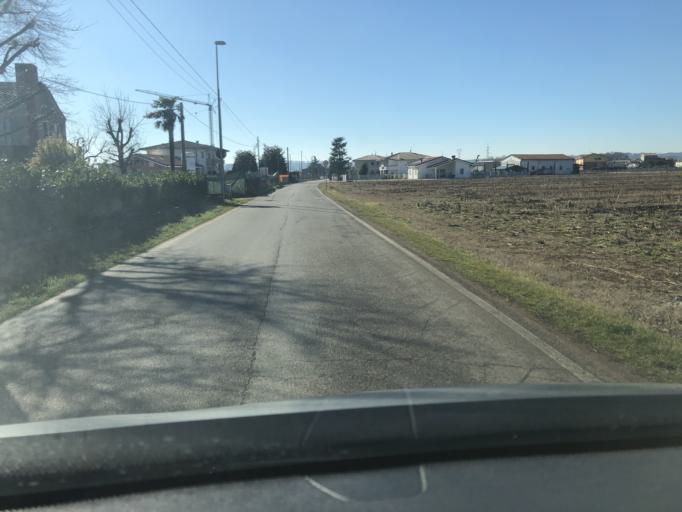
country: IT
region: Veneto
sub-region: Provincia di Verona
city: Bussolengo
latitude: 45.4575
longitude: 10.8663
